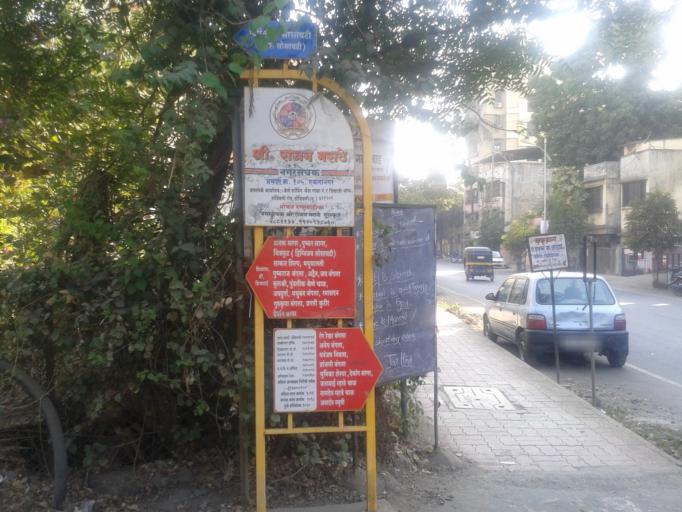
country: IN
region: Maharashtra
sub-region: Thane
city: Dombivli
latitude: 19.2052
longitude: 73.0890
